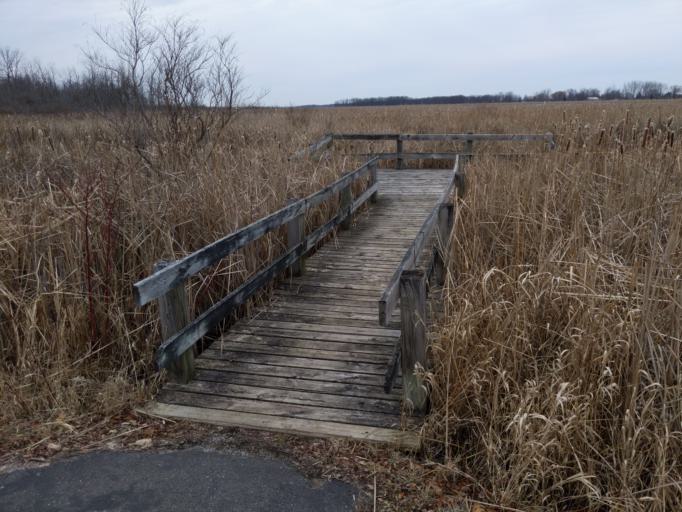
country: US
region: Michigan
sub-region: Bay County
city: Bay City
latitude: 43.6783
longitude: -83.9220
